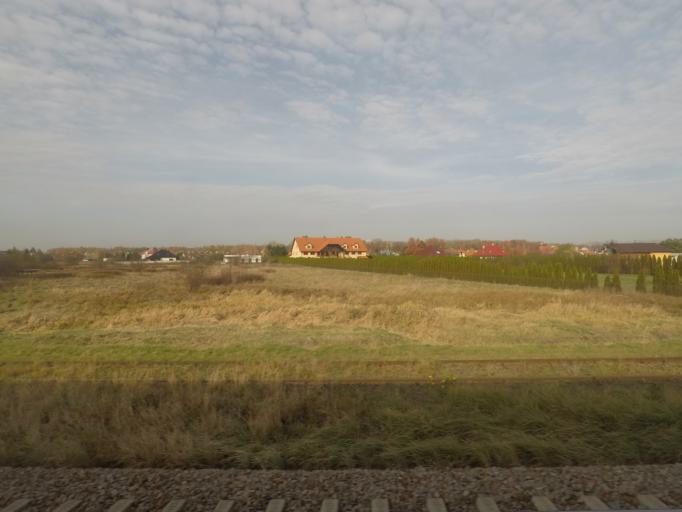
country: PL
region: Subcarpathian Voivodeship
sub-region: Powiat rzeszowski
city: Krasne
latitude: 50.0570
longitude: 22.0614
